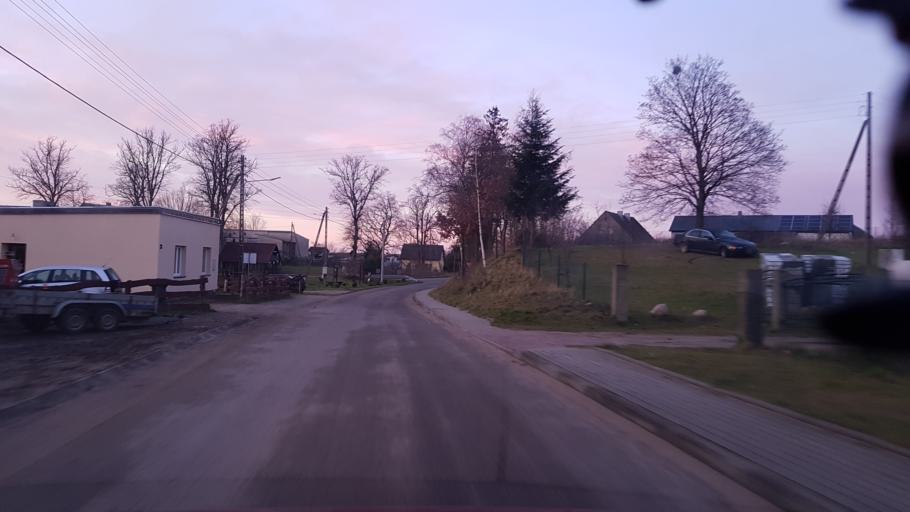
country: PL
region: Pomeranian Voivodeship
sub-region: Powiat bytowski
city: Tuchomie
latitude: 54.1326
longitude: 17.3646
